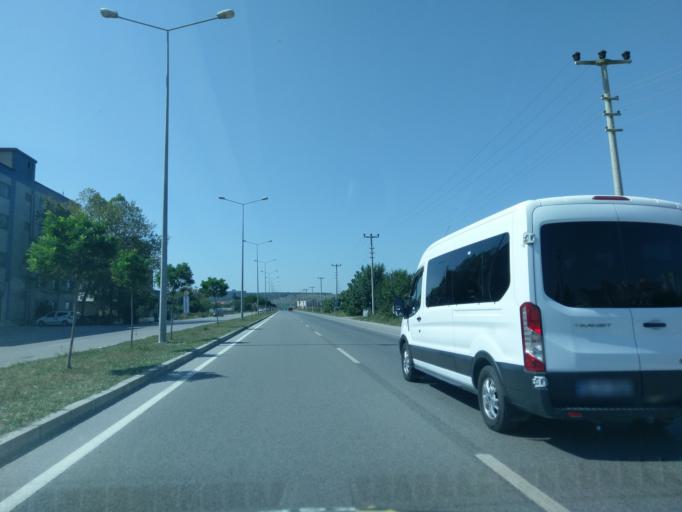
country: TR
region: Samsun
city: Bafra
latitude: 41.5735
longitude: 35.8667
